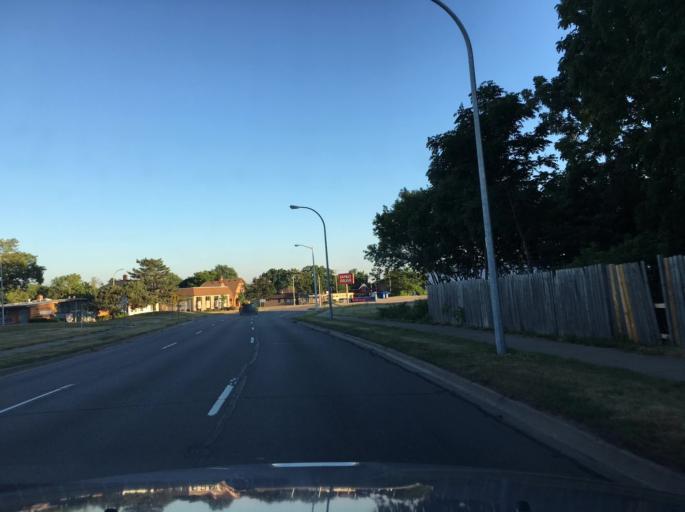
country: US
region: Michigan
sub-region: Macomb County
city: Mount Clemens
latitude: 42.5899
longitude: -82.8824
